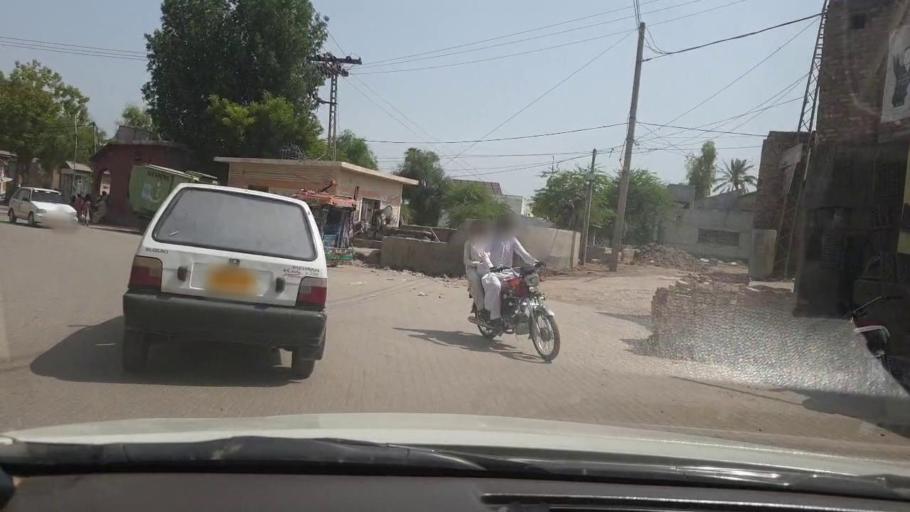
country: PK
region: Sindh
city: Shikarpur
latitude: 27.9503
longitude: 68.6294
